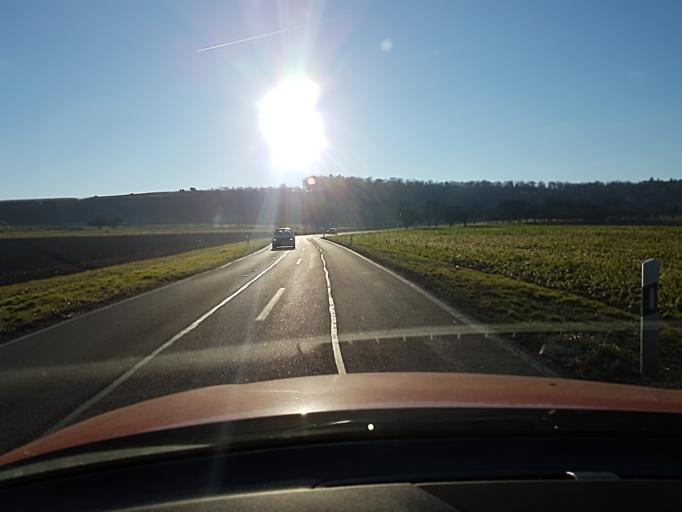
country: DE
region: Baden-Wuerttemberg
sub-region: Regierungsbezirk Stuttgart
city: Erligheim
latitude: 49.0254
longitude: 9.0804
